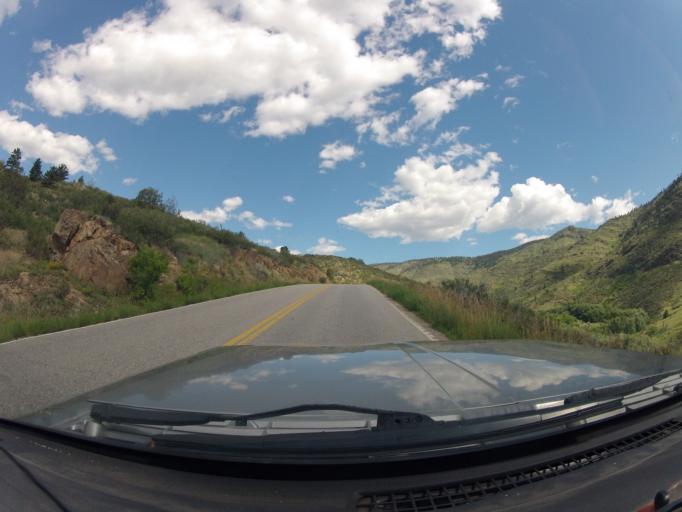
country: US
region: Colorado
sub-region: Larimer County
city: Laporte
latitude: 40.5480
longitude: -105.2877
